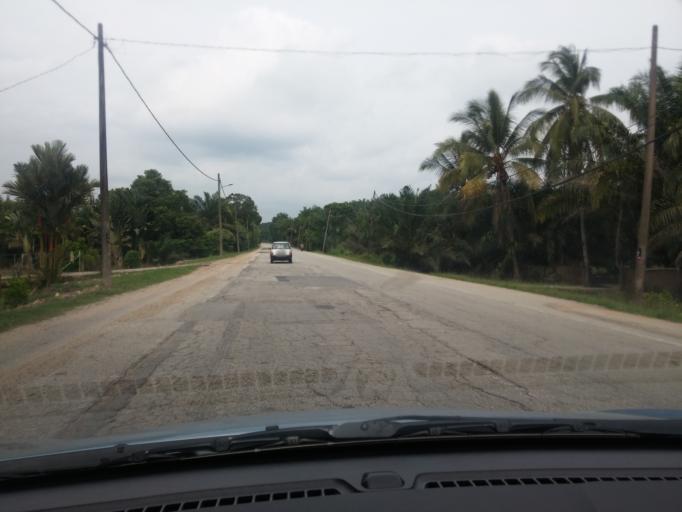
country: MY
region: Pahang
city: Kuantan
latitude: 3.8848
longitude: 103.1568
